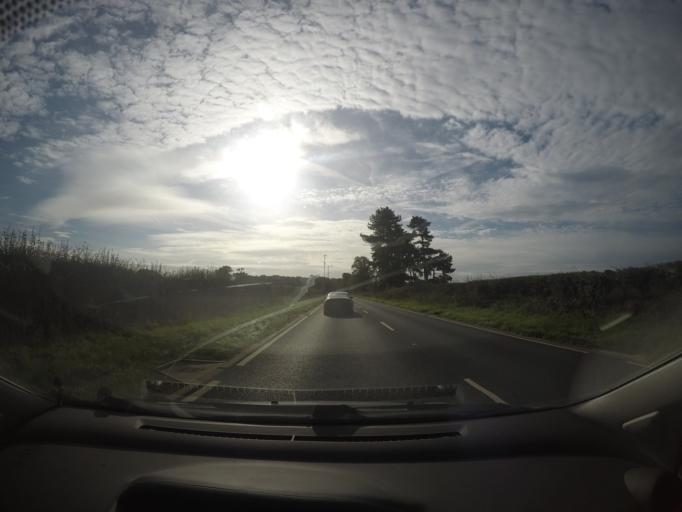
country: GB
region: England
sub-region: City of York
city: Deighton
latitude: 53.9158
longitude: -1.0553
